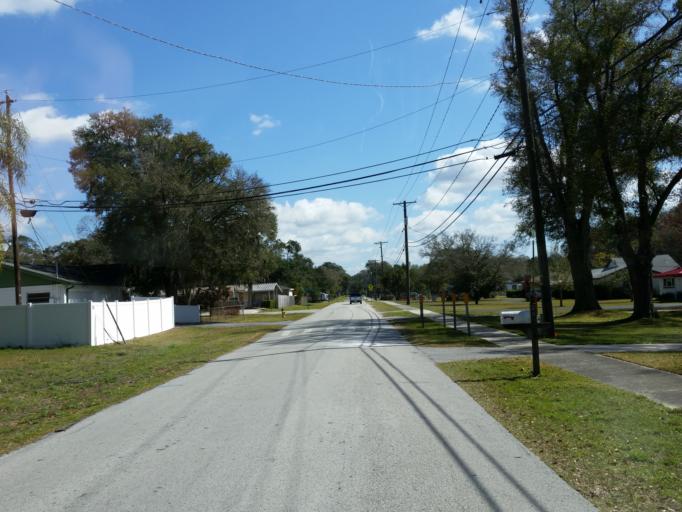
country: US
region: Florida
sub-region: Hillsborough County
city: Brandon
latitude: 27.9524
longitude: -82.2841
